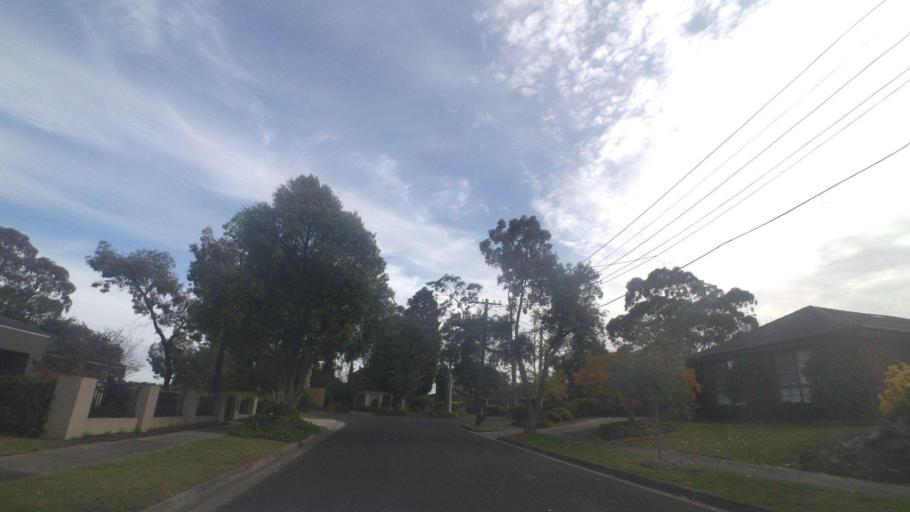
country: AU
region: Victoria
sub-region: Whitehorse
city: Vermont South
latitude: -37.8614
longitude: 145.1844
